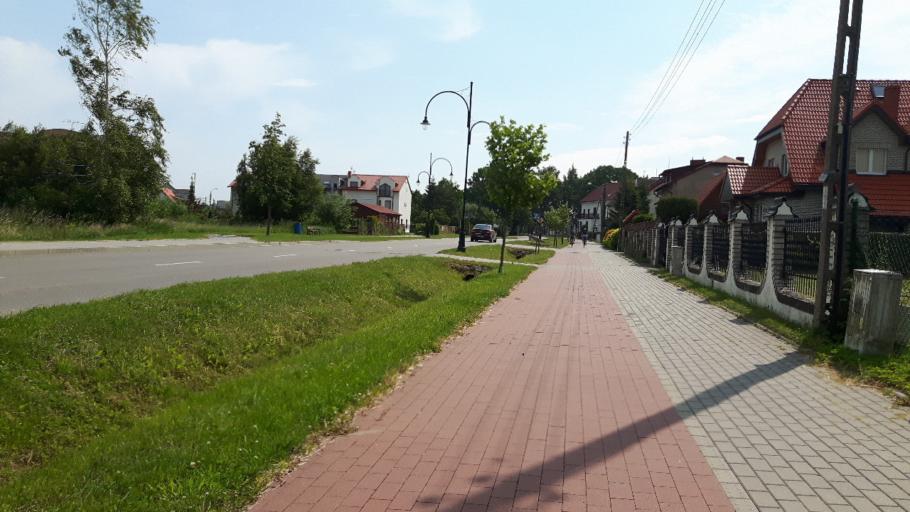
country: PL
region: Pomeranian Voivodeship
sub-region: Powiat leborski
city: Leba
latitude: 54.7499
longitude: 17.5704
